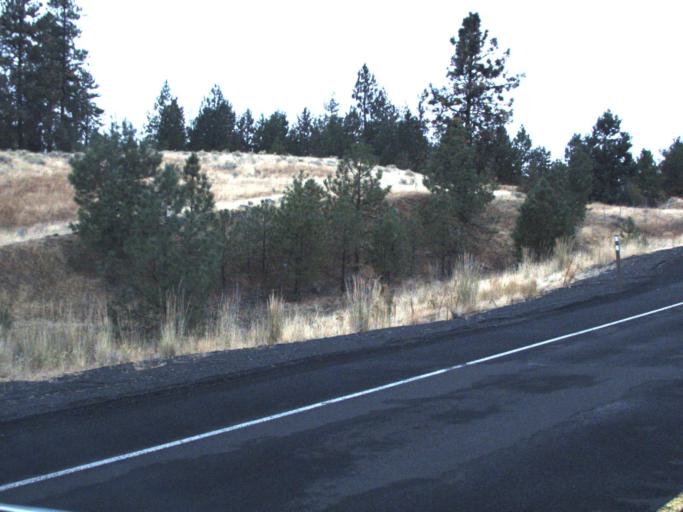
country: US
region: Washington
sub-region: Lincoln County
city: Davenport
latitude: 47.7459
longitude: -118.4766
